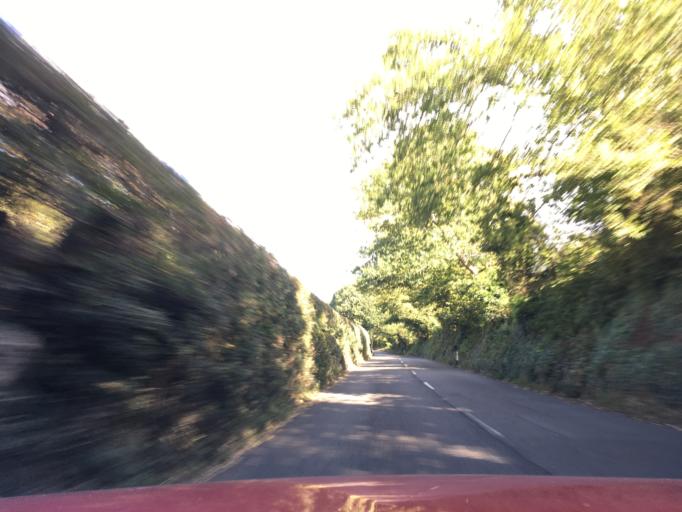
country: GB
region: England
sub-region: Devon
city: Newton Poppleford
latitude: 50.7007
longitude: -3.2809
